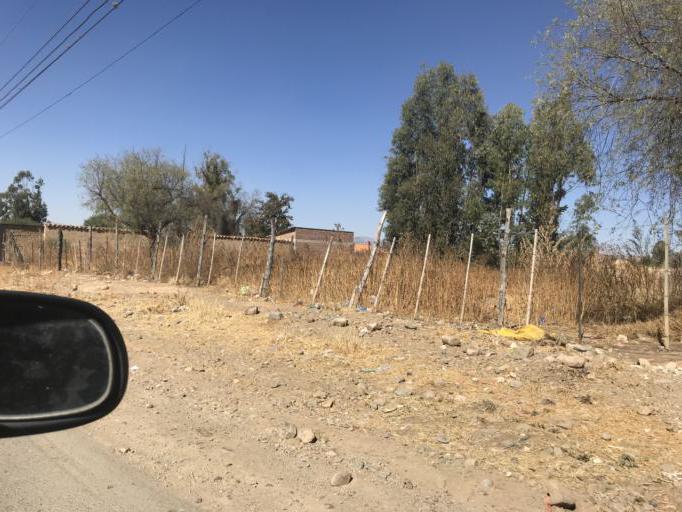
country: BO
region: Cochabamba
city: Tarata
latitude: -17.6035
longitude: -65.9868
